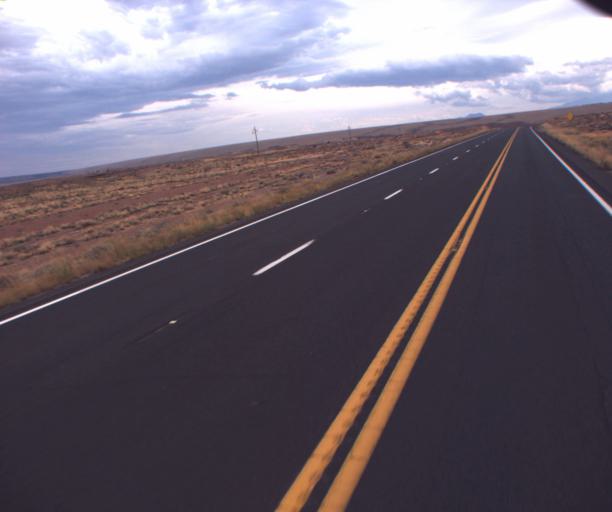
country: US
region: Arizona
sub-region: Coconino County
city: Tuba City
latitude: 35.8019
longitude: -111.4462
